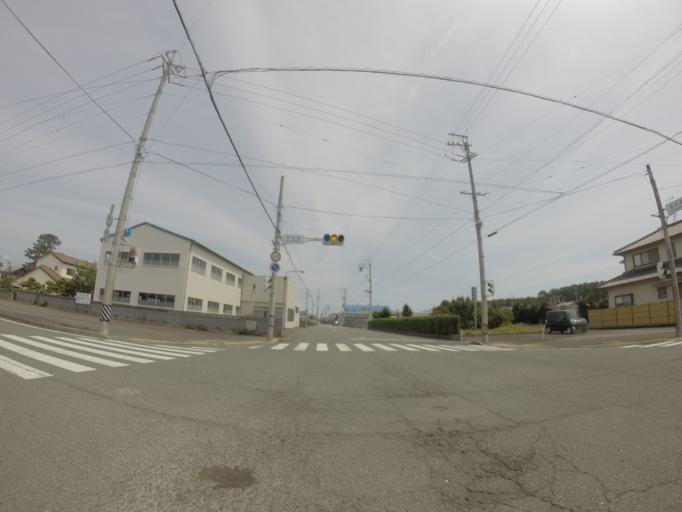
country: JP
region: Shizuoka
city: Yaizu
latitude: 34.7913
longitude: 138.3048
